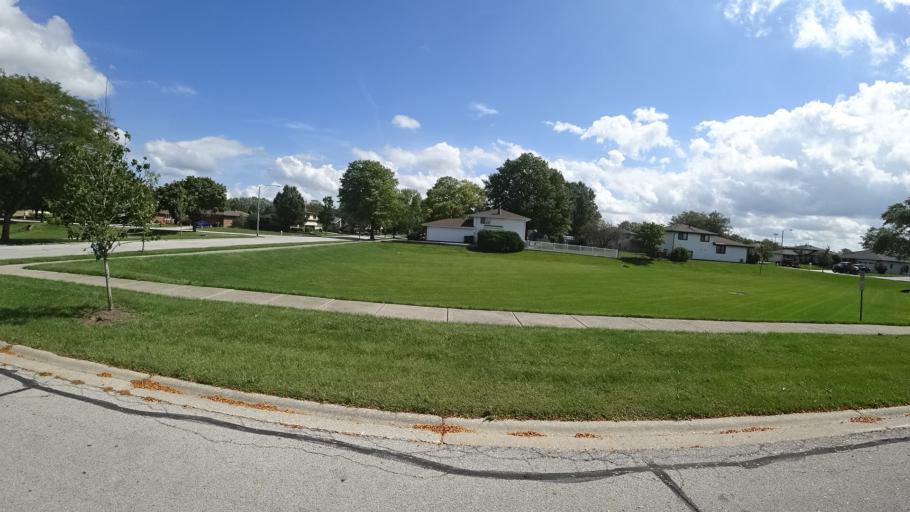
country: US
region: Illinois
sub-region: Cook County
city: Tinley Park
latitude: 41.5622
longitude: -87.7770
